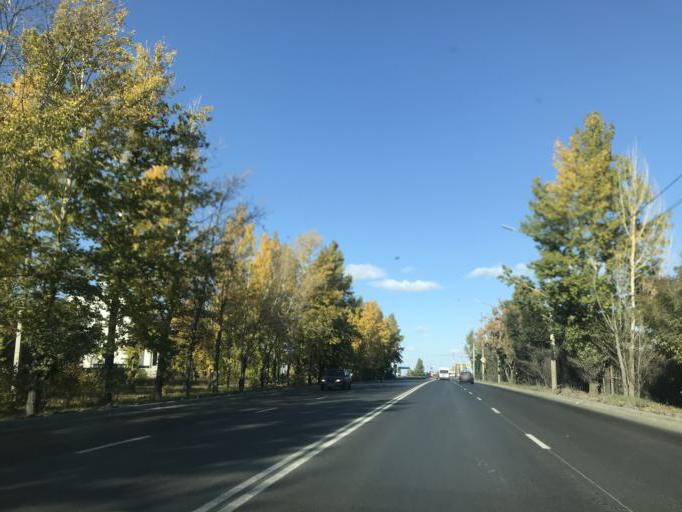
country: RU
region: Chelyabinsk
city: Roshchino
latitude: 55.2386
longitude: 61.3181
